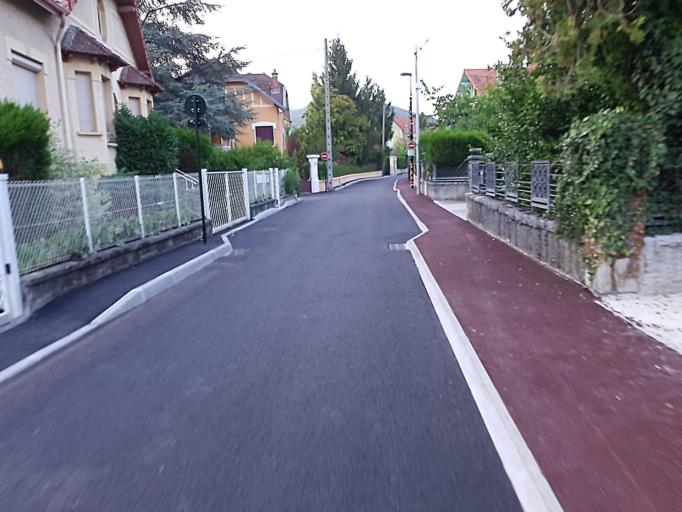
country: FR
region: Rhone-Alpes
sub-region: Departement de la Savoie
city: Tresserve
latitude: 45.6973
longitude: 5.9028
